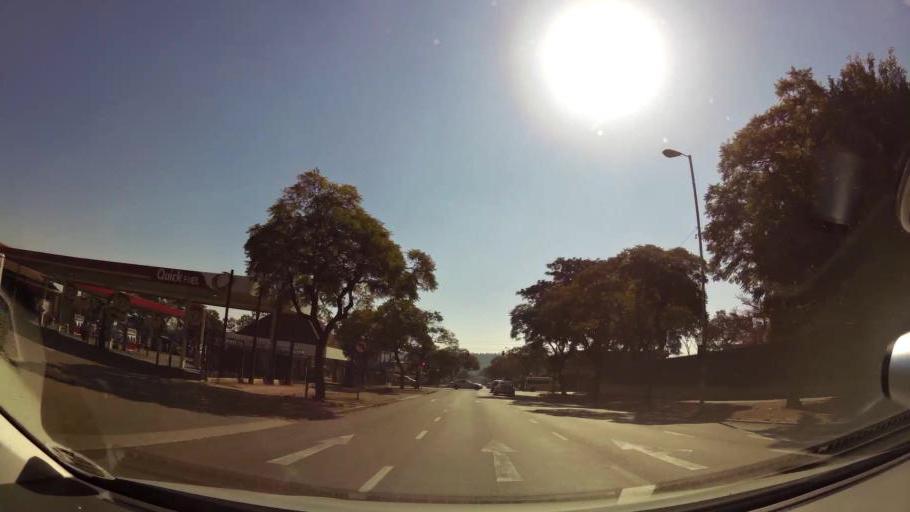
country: ZA
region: Gauteng
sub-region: City of Tshwane Metropolitan Municipality
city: Pretoria
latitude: -25.7430
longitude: 28.1804
